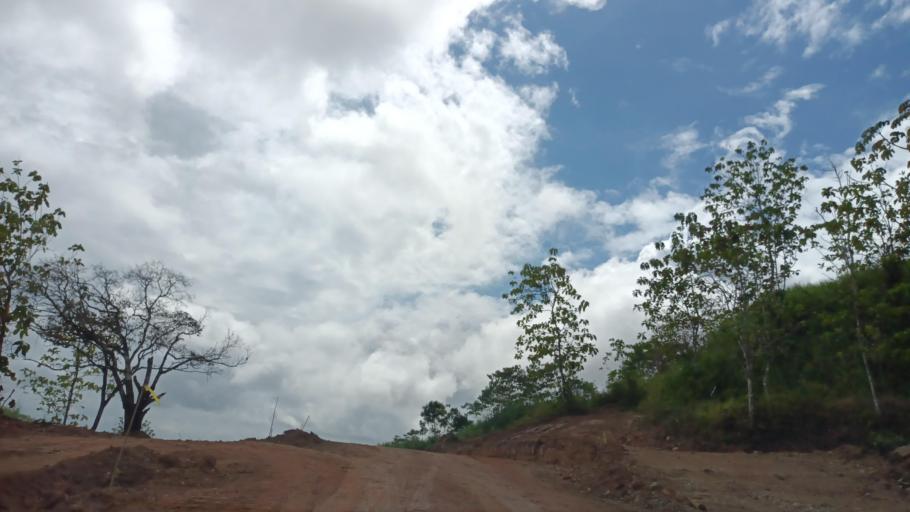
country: PA
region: Panama
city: La Cabima
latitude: 9.1159
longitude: -79.4978
